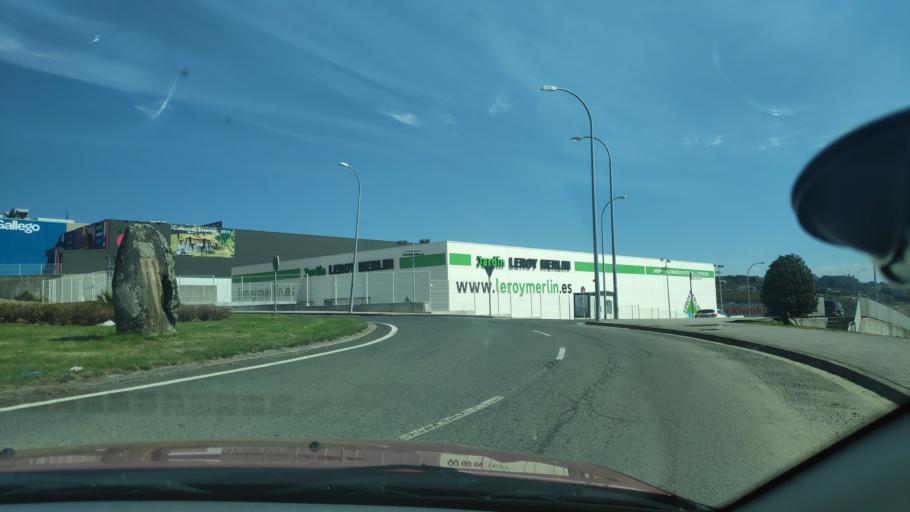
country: ES
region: Galicia
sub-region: Provincia da Coruna
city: Santiago de Compostela
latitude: 42.9025
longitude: -8.5102
